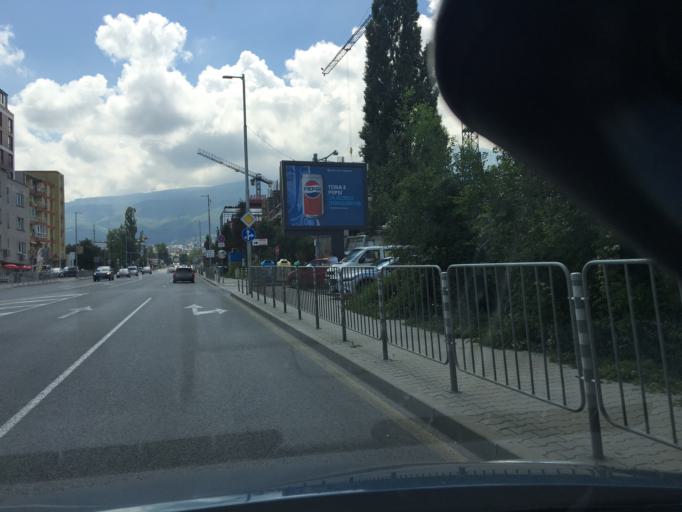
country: BG
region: Sofia-Capital
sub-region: Stolichna Obshtina
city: Sofia
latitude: 42.6497
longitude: 23.3154
